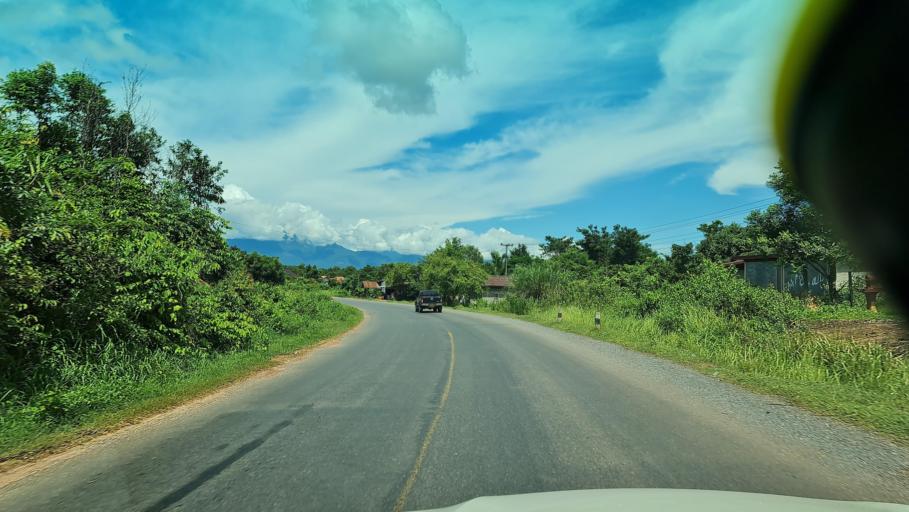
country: LA
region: Bolikhamxai
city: Pakkading
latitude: 18.2796
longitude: 104.0652
